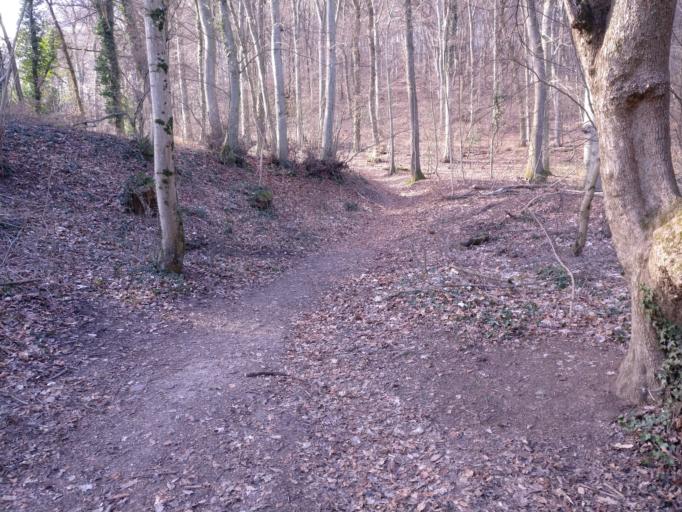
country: DE
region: Baden-Wuerttemberg
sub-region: Karlsruhe Region
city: Heidelberg
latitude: 49.4191
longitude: 8.7109
